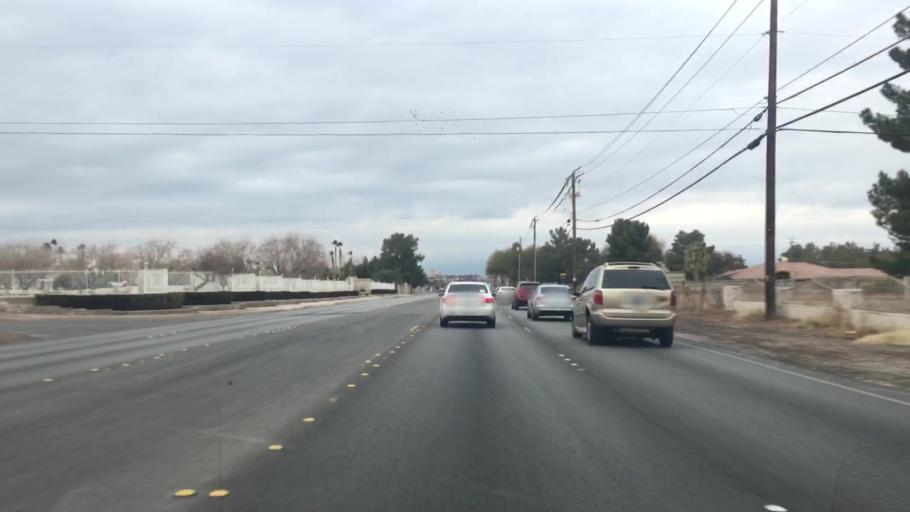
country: US
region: Nevada
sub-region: Clark County
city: Whitney
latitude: 36.0677
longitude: -115.1006
